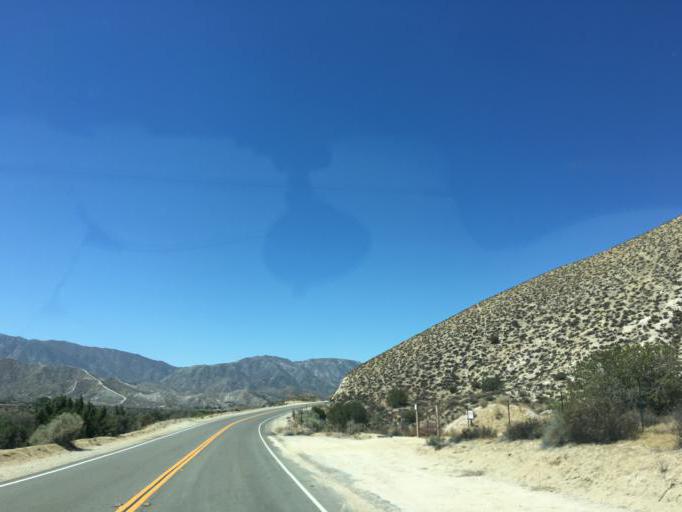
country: US
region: California
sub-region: Los Angeles County
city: Acton
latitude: 34.4514
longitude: -118.2035
